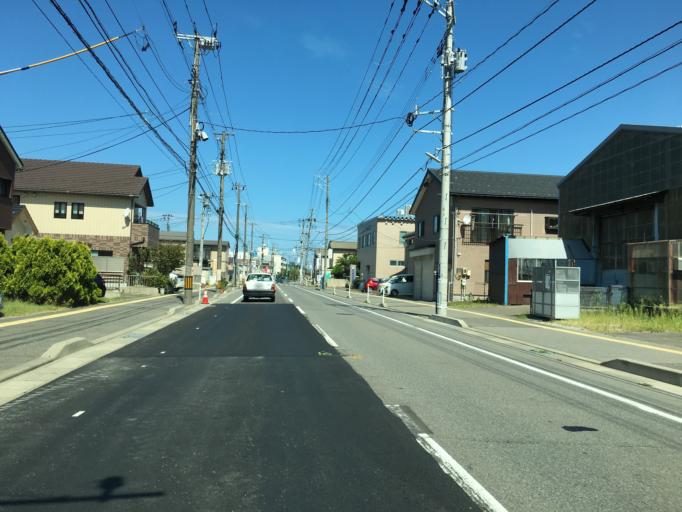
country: JP
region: Niigata
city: Niigata-shi
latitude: 37.9340
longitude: 139.0570
